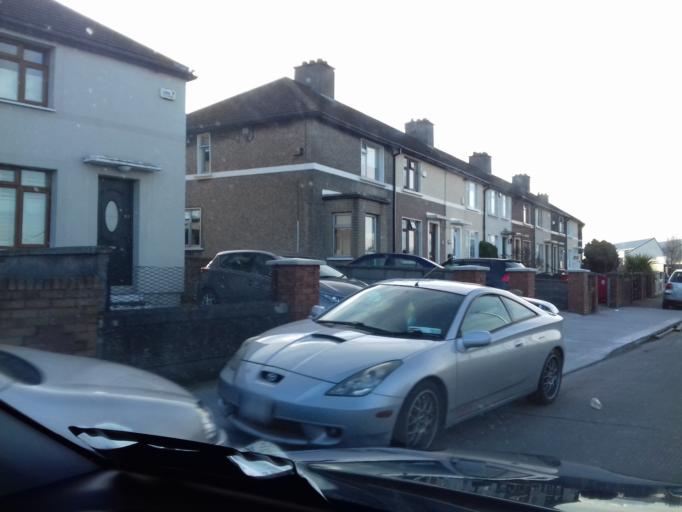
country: IE
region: Leinster
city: Cabra
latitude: 53.3696
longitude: -6.2905
